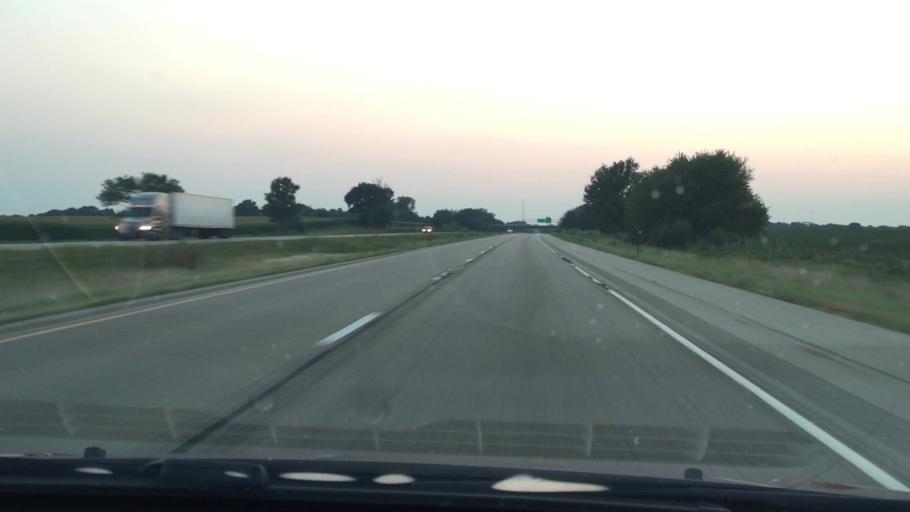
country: US
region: Illinois
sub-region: Bureau County
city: Depue
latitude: 41.4000
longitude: -89.3470
